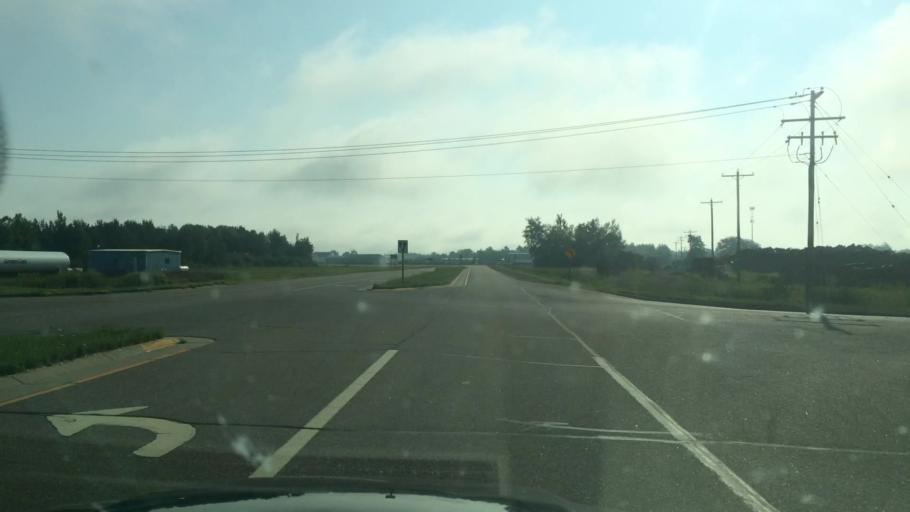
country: US
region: Wisconsin
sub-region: Langlade County
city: Antigo
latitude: 45.1549
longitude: -89.1677
